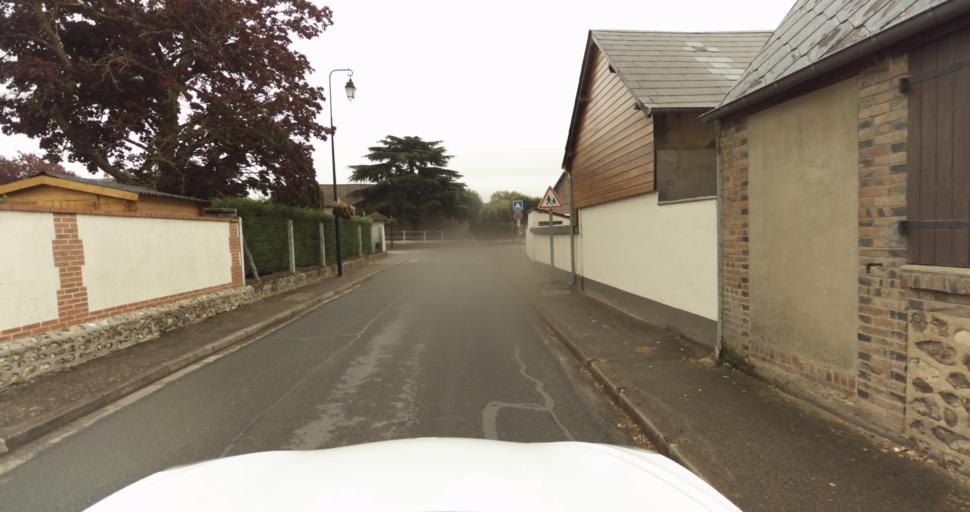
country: FR
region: Haute-Normandie
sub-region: Departement de l'Eure
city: Aviron
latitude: 49.0840
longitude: 1.0725
